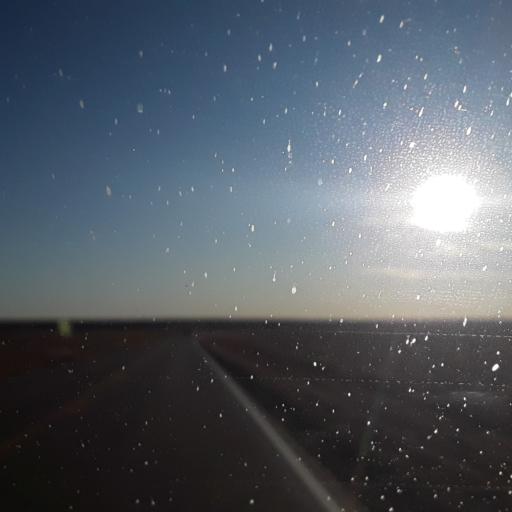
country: US
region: Kansas
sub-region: Wallace County
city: Sharon Springs
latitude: 38.9582
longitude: -101.7435
